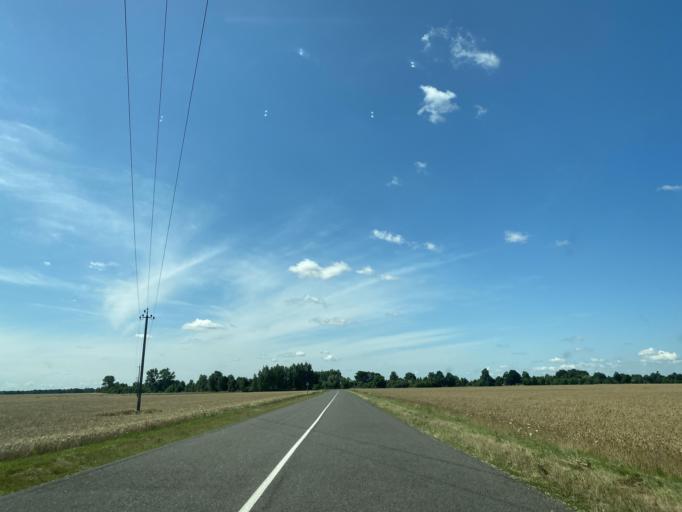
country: BY
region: Brest
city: Ivanava
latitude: 52.2065
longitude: 25.6197
